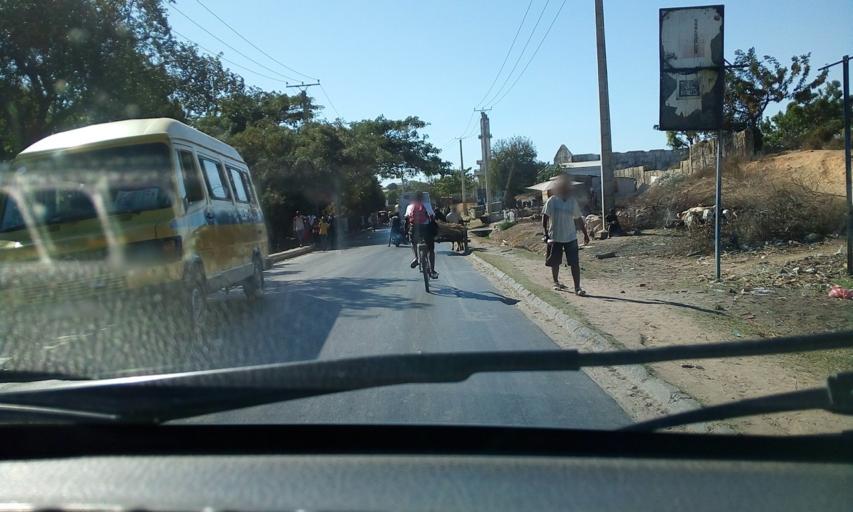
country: MG
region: Boeny
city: Mahajanga
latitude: -15.7184
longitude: 46.3310
